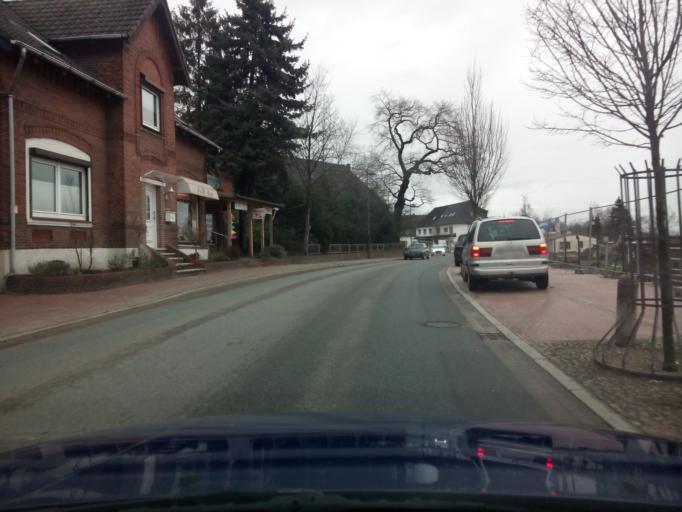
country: DE
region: Lower Saxony
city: Ritterhude
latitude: 53.1801
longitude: 8.7535
